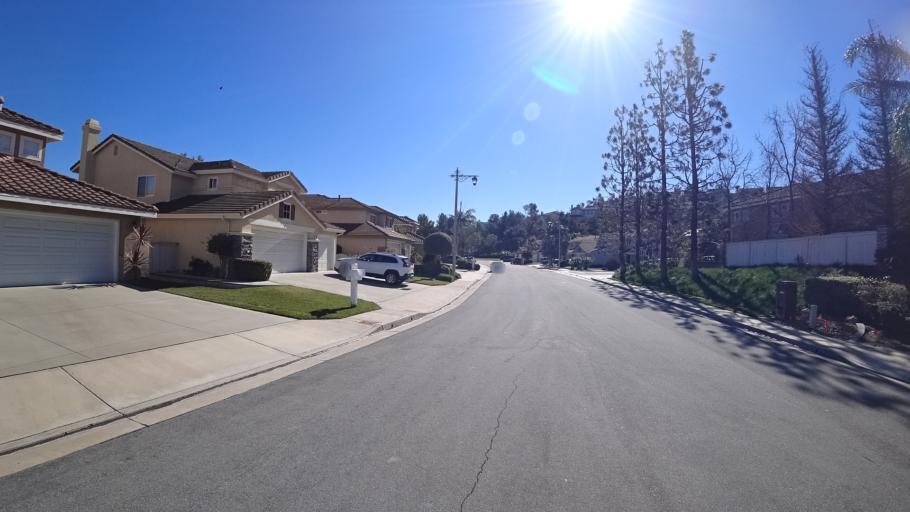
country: US
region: California
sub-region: Orange County
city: Yorba Linda
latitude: 33.8546
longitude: -117.7331
